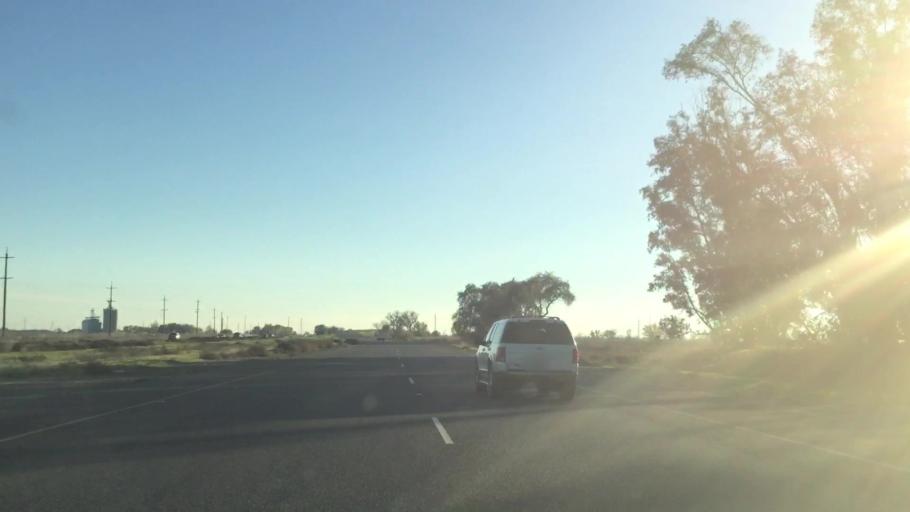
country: US
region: California
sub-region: Yuba County
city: Plumas Lake
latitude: 38.8621
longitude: -121.5436
